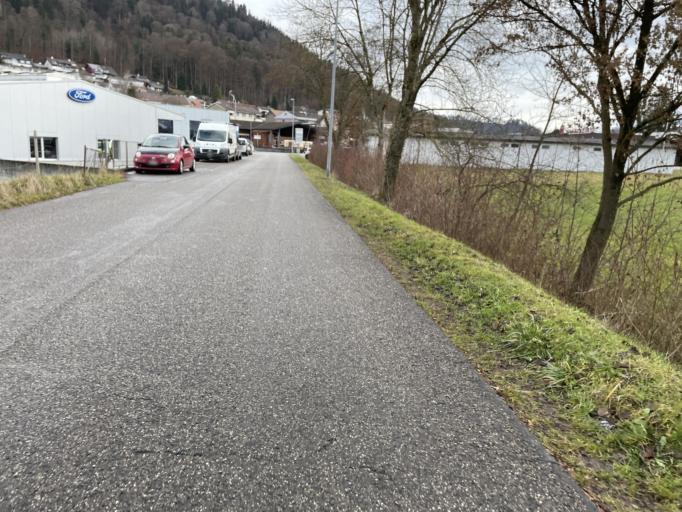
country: CH
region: Bern
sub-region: Thun District
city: Heimberg
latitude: 46.7978
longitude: 7.6018
